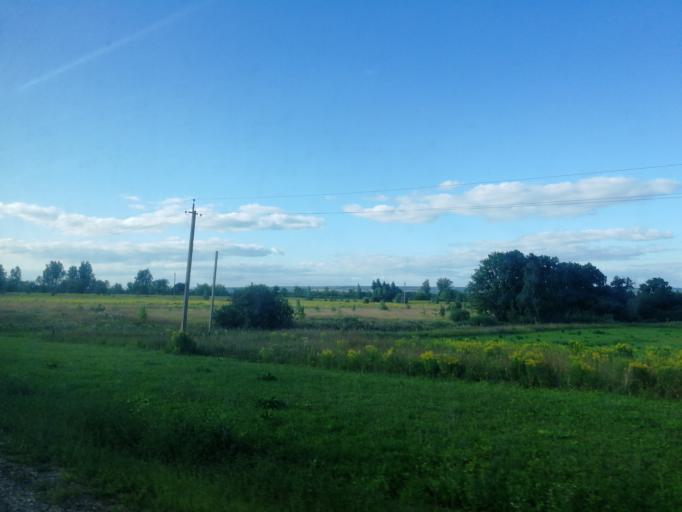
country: RU
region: Tula
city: Leninskiy
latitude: 54.2455
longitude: 37.3271
